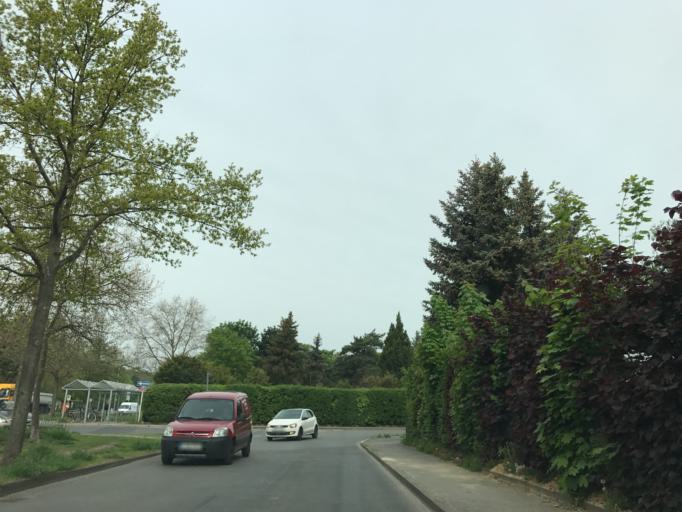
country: DE
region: Berlin
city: Staaken
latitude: 52.5240
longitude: 13.1455
